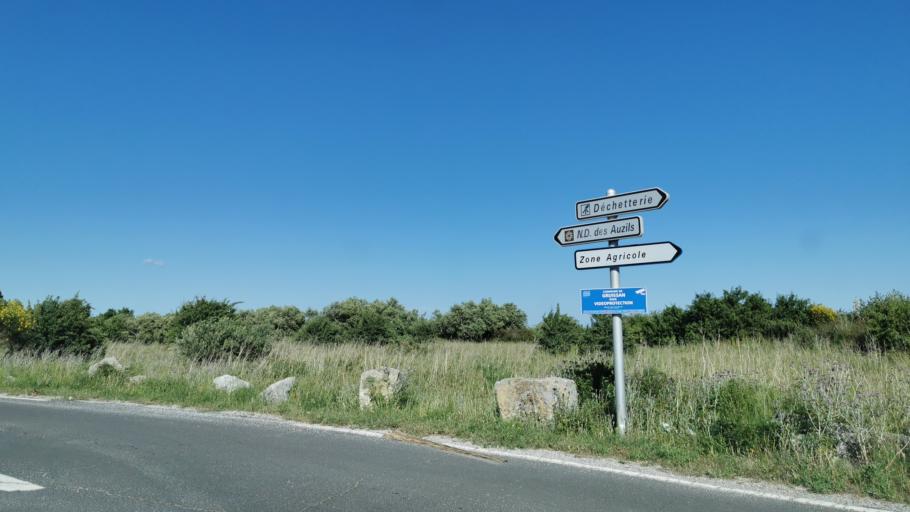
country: FR
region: Languedoc-Roussillon
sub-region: Departement de l'Aude
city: Gruissan
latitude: 43.1198
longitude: 3.0945
